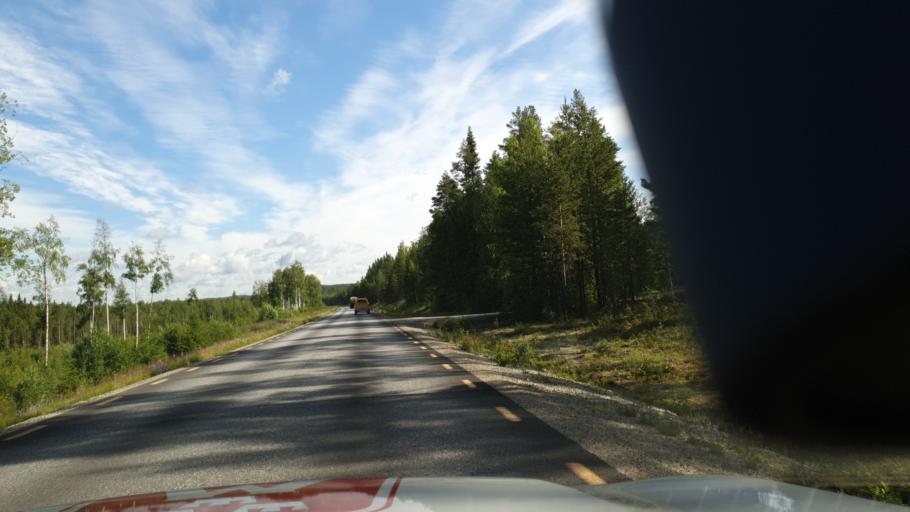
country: SE
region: Vaesterbotten
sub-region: Norsjo Kommun
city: Norsjoe
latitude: 64.5077
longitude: 19.3373
